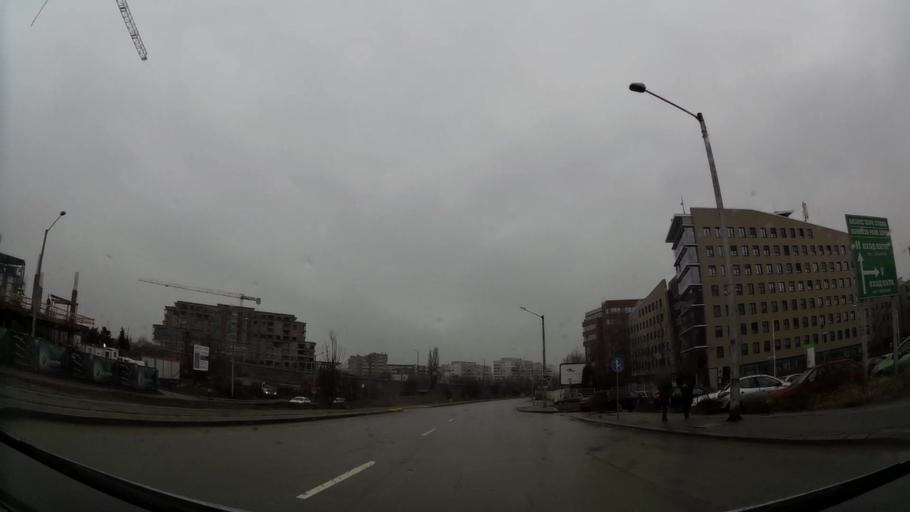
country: BG
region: Sofia-Capital
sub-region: Stolichna Obshtina
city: Sofia
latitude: 42.6248
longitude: 23.3743
